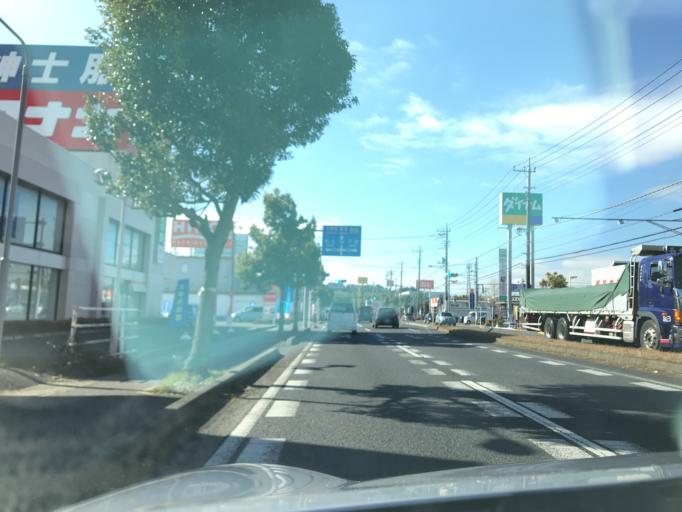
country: JP
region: Chiba
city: Mobara
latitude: 35.4380
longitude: 140.2880
